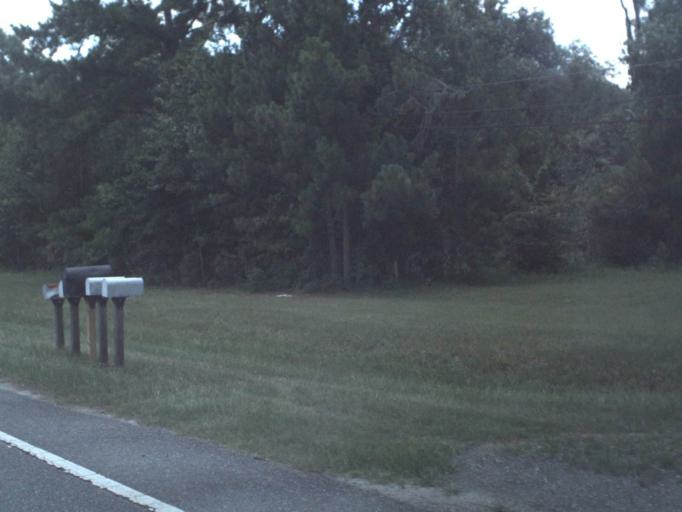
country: US
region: Florida
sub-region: Columbia County
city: Lake City
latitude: 30.1436
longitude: -82.6367
